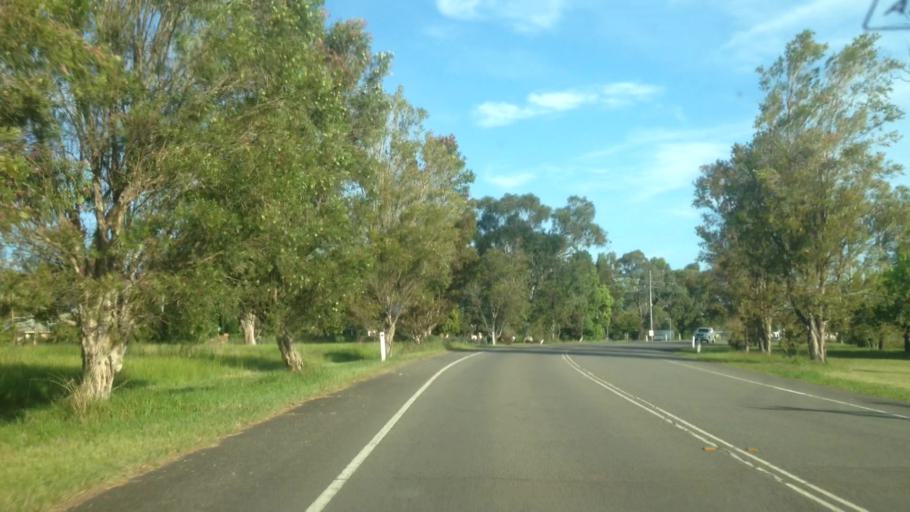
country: AU
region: New South Wales
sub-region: Lake Macquarie Shire
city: Dora Creek
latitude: -33.1023
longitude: 151.4766
